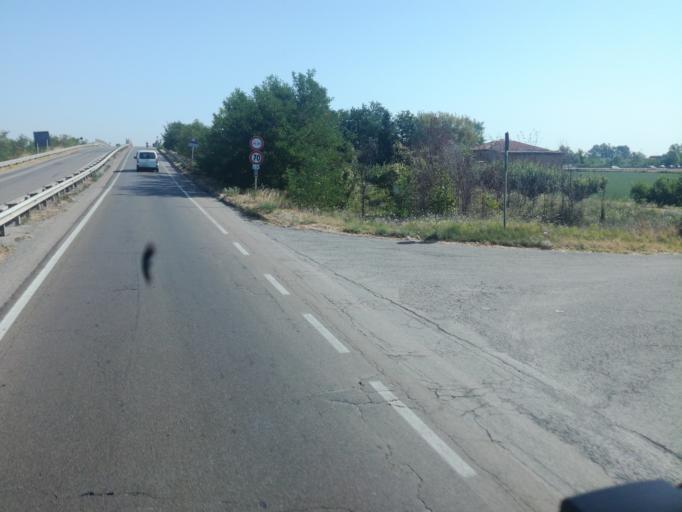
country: IT
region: Emilia-Romagna
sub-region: Provincia di Bologna
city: Castel San Pietro Terme
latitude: 44.4253
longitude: 11.6030
